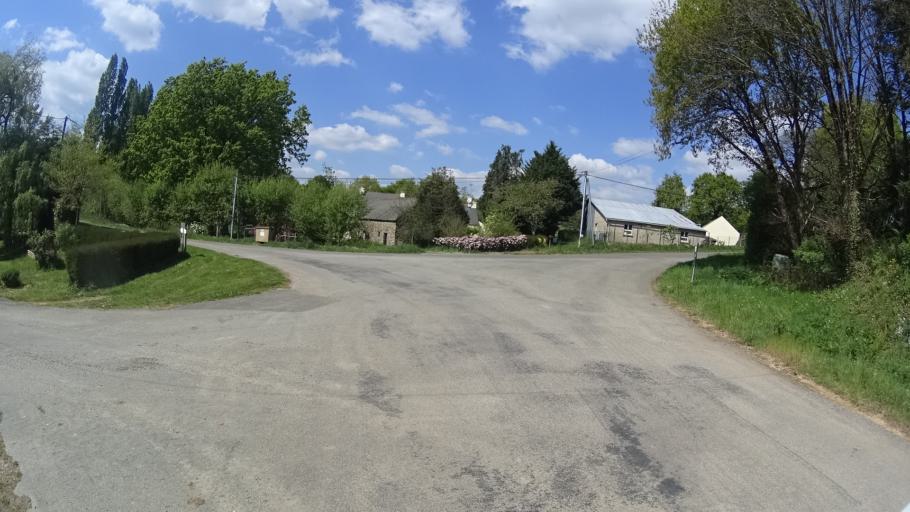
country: FR
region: Brittany
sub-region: Departement du Morbihan
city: Beganne
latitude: 47.5827
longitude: -2.2694
